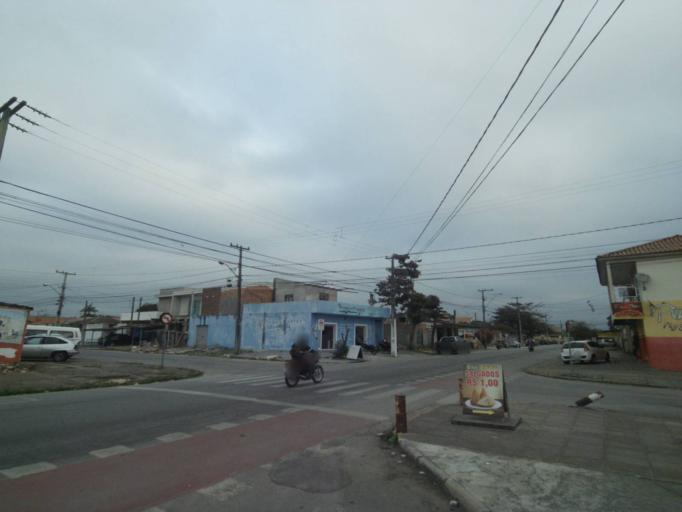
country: BR
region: Parana
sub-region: Paranagua
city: Paranagua
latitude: -25.5192
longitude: -48.5219
